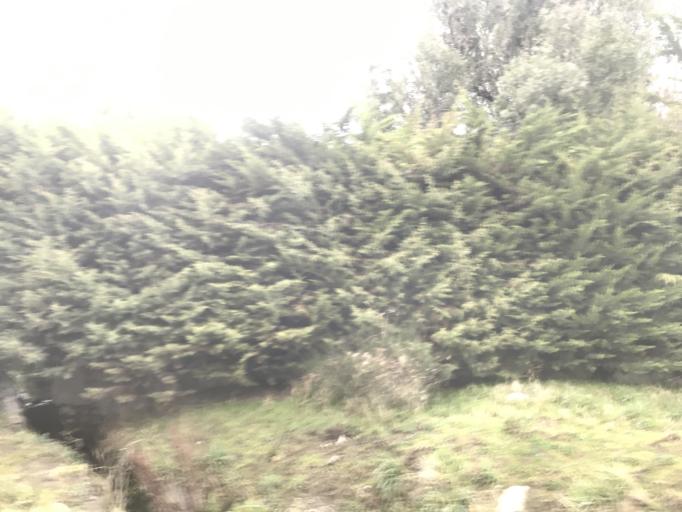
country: AR
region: Rio Negro
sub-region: Departamento de Bariloche
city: San Carlos de Bariloche
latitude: -41.1325
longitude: -71.3547
